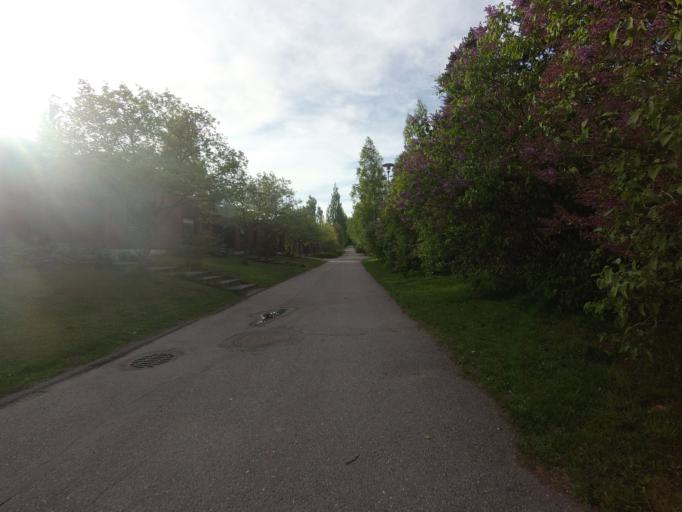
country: FI
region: Uusimaa
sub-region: Helsinki
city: Koukkuniemi
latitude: 60.1513
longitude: 24.7528
